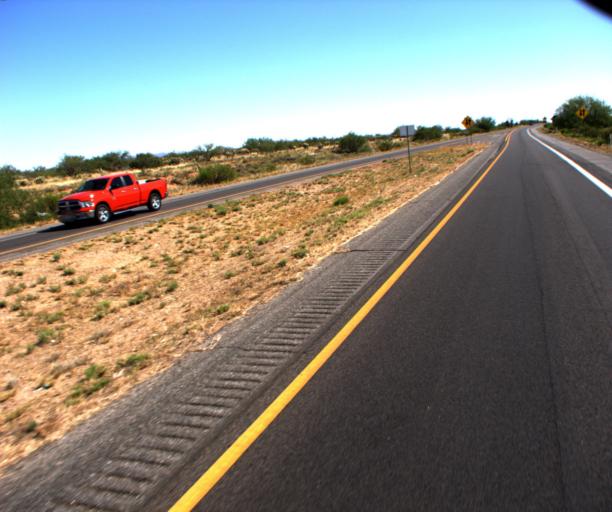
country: US
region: Arizona
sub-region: Pima County
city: Catalina
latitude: 32.5603
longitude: -110.9309
